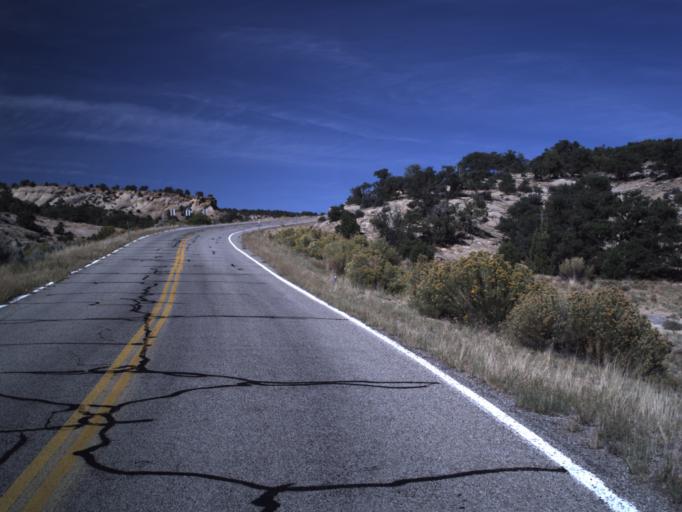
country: US
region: Utah
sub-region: San Juan County
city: Monticello
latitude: 37.9864
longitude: -109.4981
